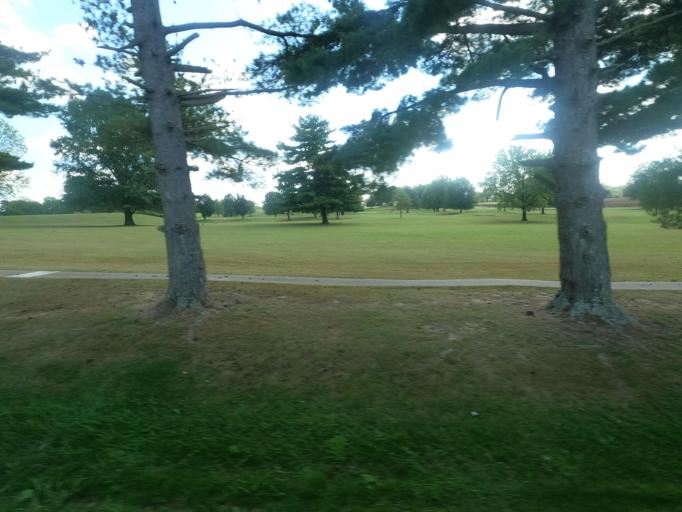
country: US
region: Illinois
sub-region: Massac County
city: Metropolis
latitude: 37.1914
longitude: -88.7028
